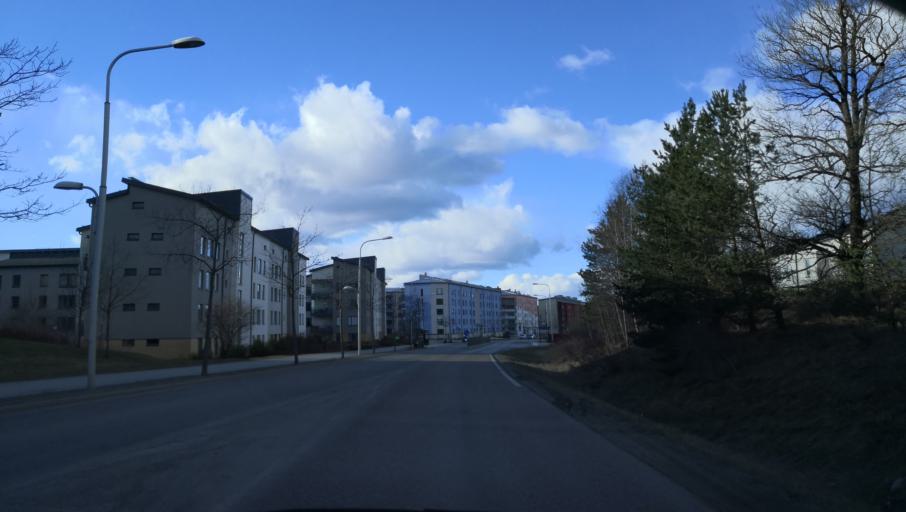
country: SE
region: Stockholm
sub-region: Varmdo Kommun
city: Gustavsberg
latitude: 59.3182
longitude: 18.3893
